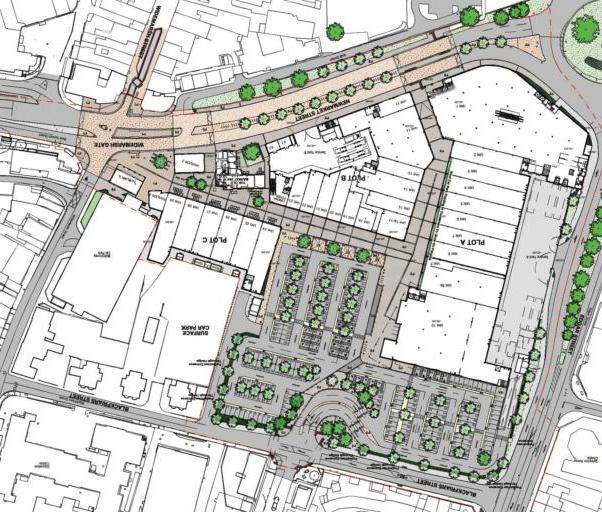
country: GB
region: England
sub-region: Herefordshire
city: Hereford
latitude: 52.0591
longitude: -2.7180
